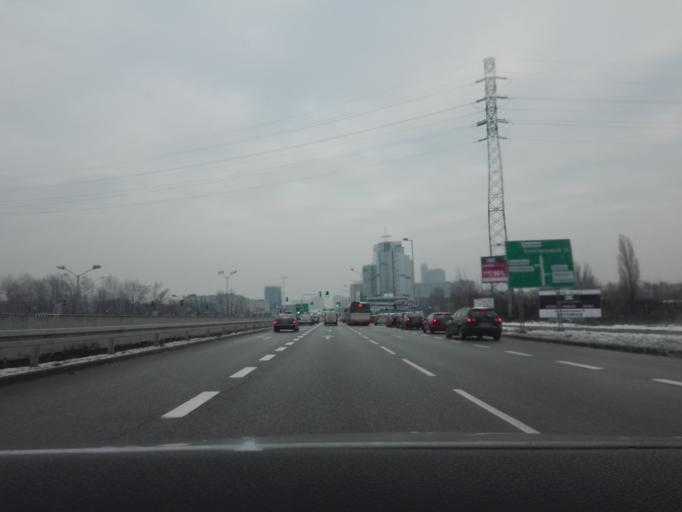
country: PL
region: Silesian Voivodeship
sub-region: Katowice
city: Katowice
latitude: 50.2673
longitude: 19.0099
